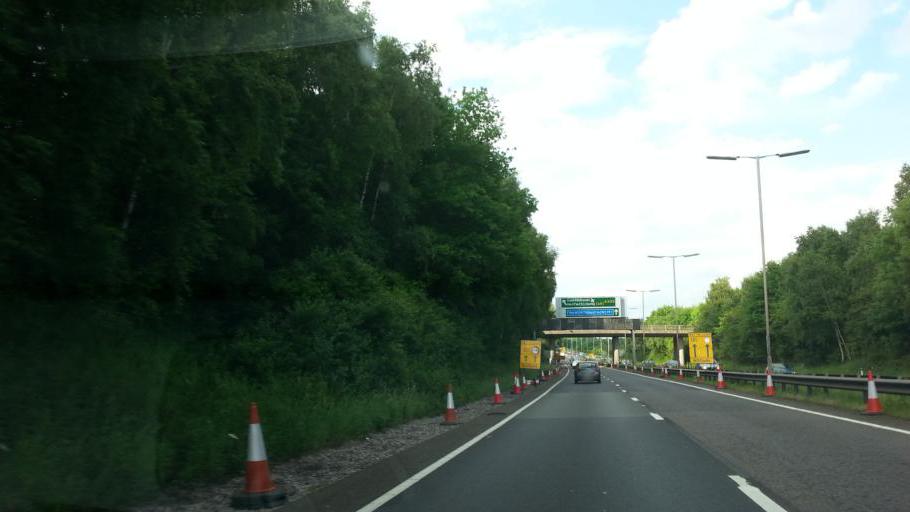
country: GB
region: England
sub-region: Leicestershire
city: Kegworth
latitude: 52.8095
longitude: -1.3150
